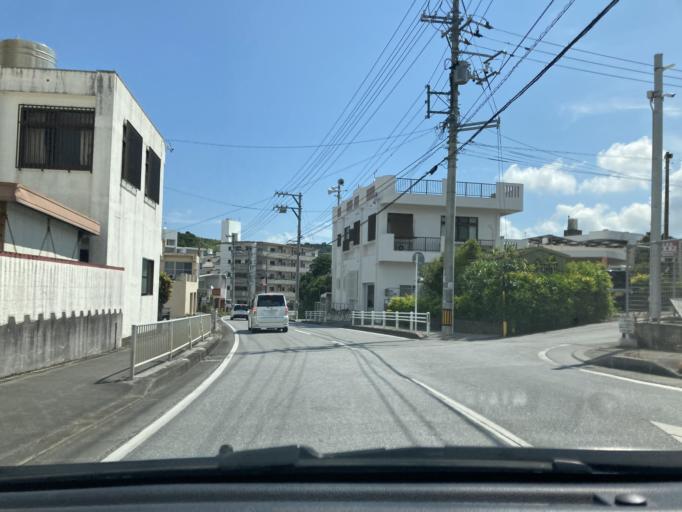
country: JP
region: Okinawa
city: Tomigusuku
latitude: 26.1772
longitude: 127.7457
